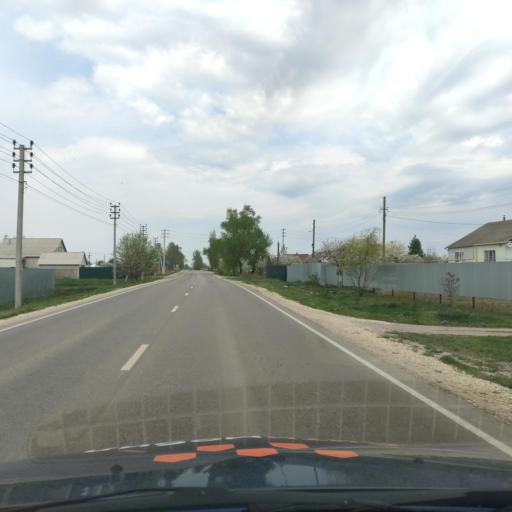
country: RU
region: Voronezj
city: Podgornoye
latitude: 51.8763
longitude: 39.1731
